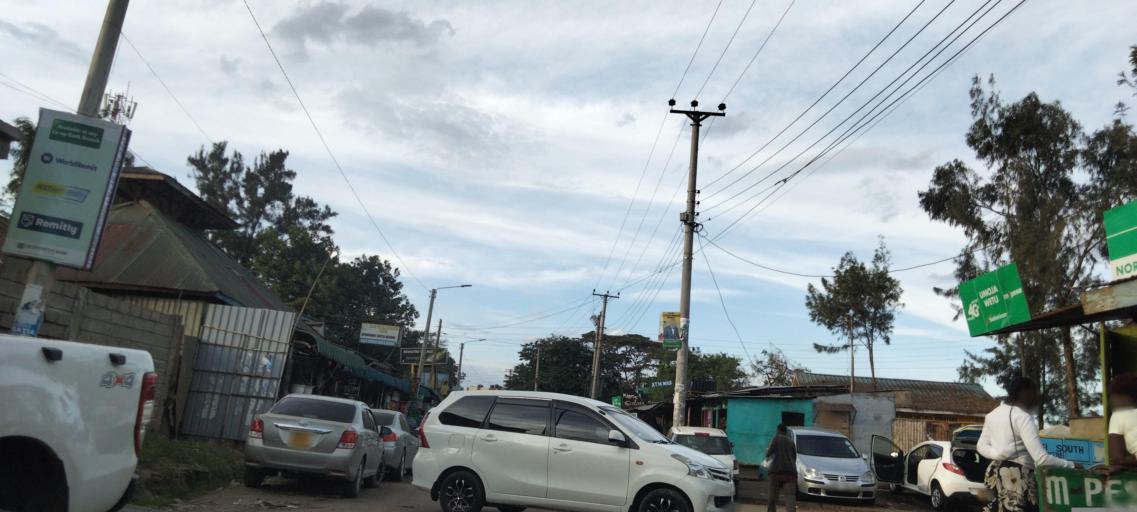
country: KE
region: Nairobi Area
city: Pumwani
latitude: -1.2685
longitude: 36.8825
